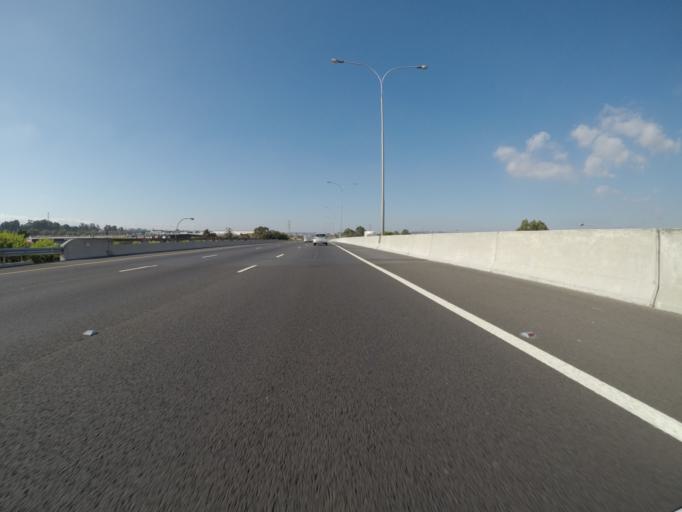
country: ZA
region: Western Cape
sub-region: City of Cape Town
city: Kraaifontein
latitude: -33.9146
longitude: 18.6683
